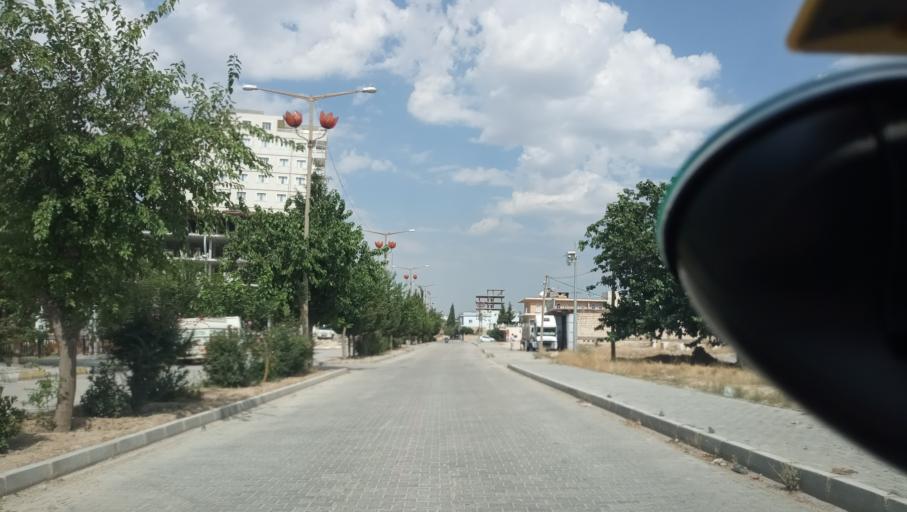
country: TR
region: Mardin
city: Yesilli
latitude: 37.3396
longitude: 40.8158
